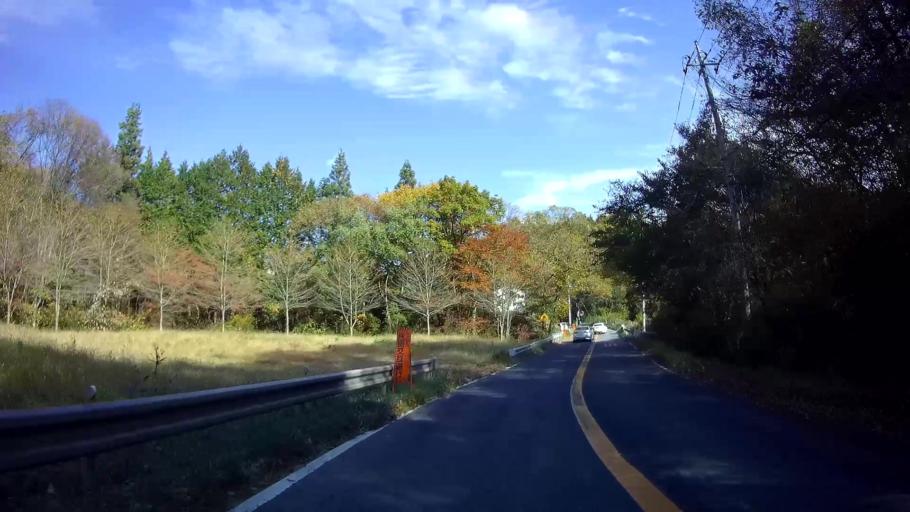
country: JP
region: Gunma
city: Nakanojomachi
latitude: 36.4928
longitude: 138.7744
